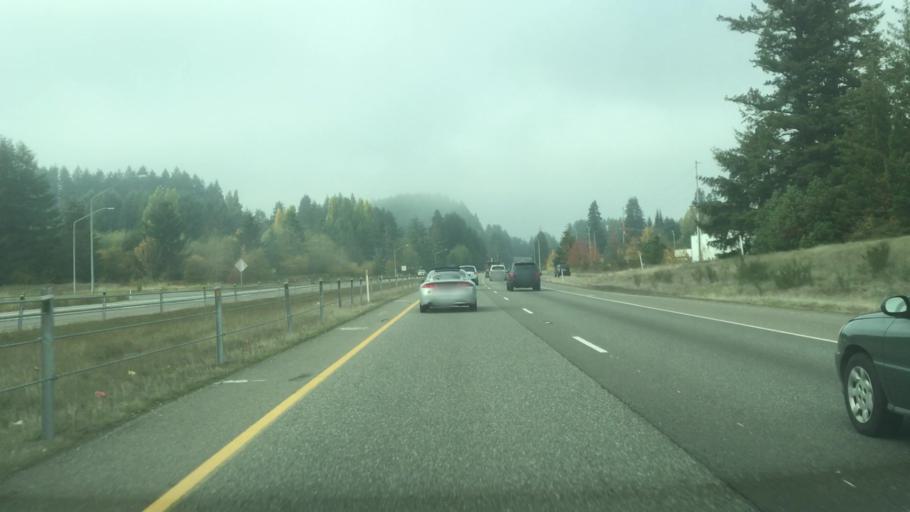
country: US
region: Washington
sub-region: Thurston County
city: Tumwater
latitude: 47.0477
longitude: -122.9953
